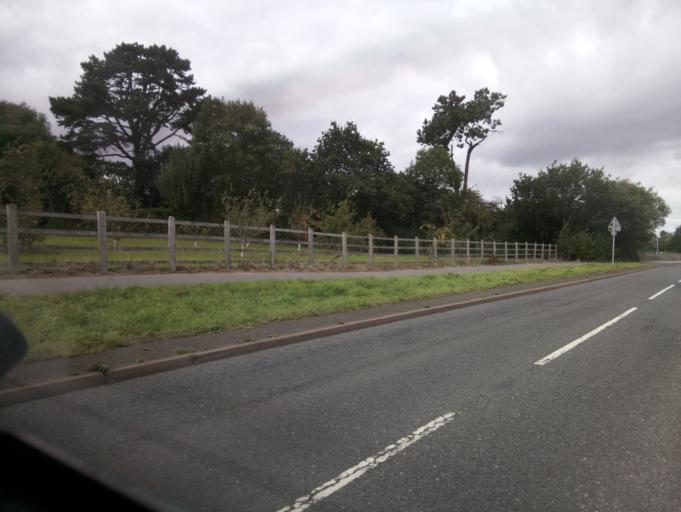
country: GB
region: England
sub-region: Devon
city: Starcross
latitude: 50.6195
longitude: -3.4475
